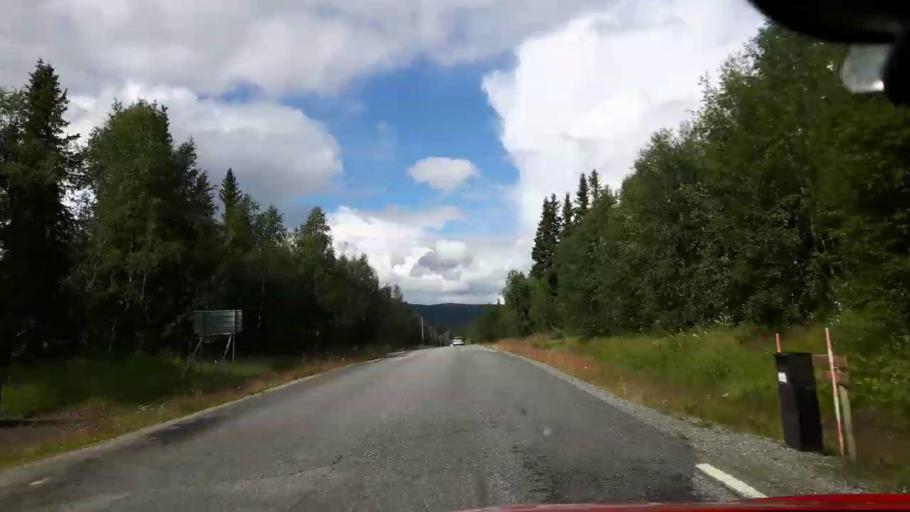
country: NO
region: Nordland
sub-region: Hattfjelldal
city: Hattfjelldal
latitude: 65.0617
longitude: 14.8856
